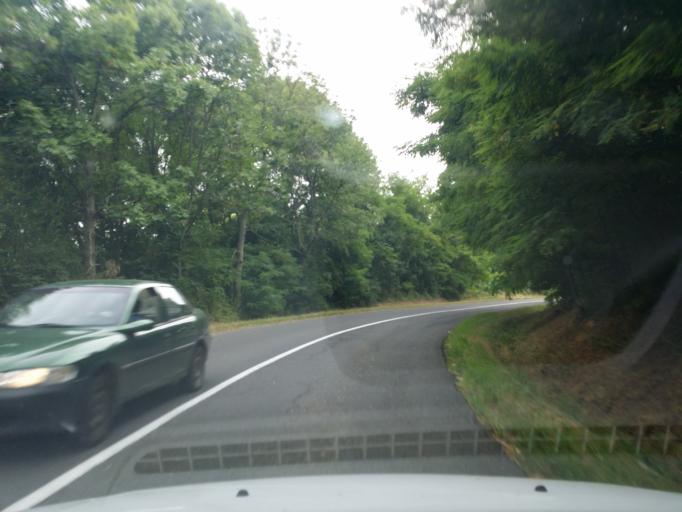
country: HU
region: Nograd
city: Bercel
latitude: 47.9213
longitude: 19.3675
